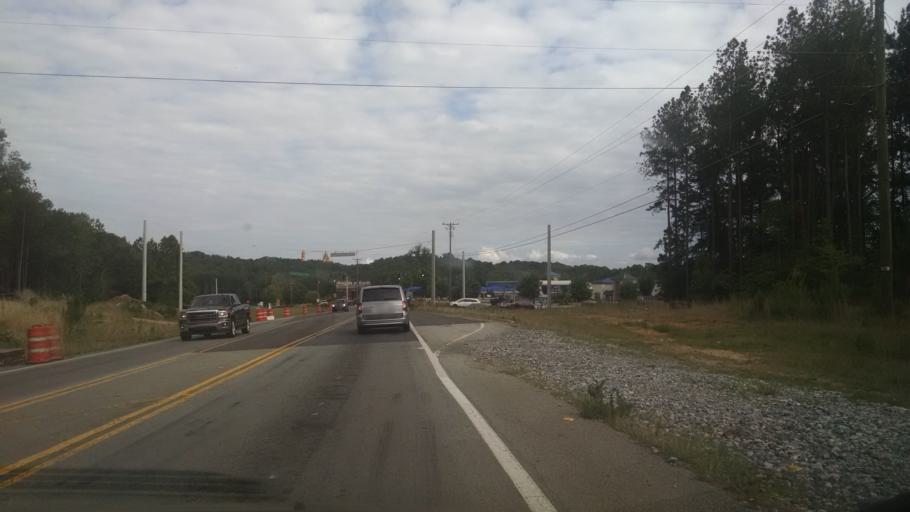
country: US
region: Georgia
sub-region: Gwinnett County
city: Sugar Hill
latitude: 34.1306
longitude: -84.0982
